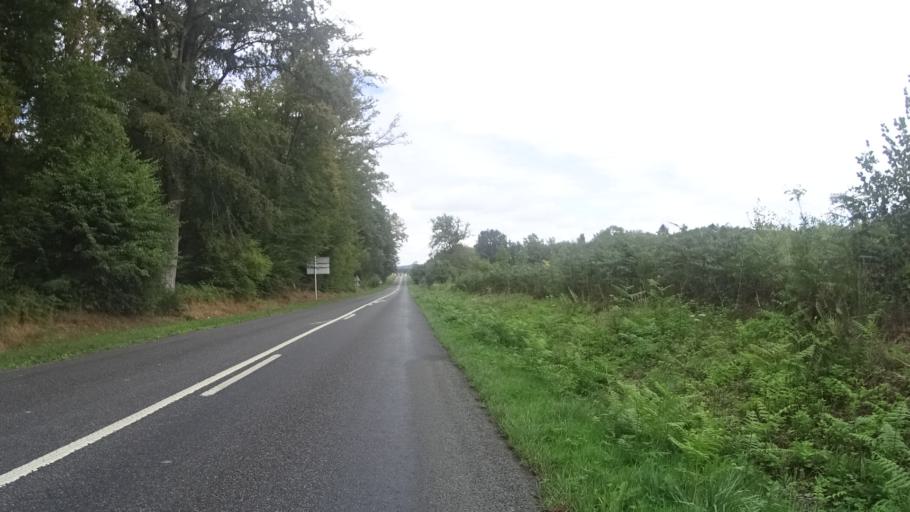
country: FR
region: Picardie
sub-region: Departement de l'Oise
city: Noyon
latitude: 49.5495
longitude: 2.9869
